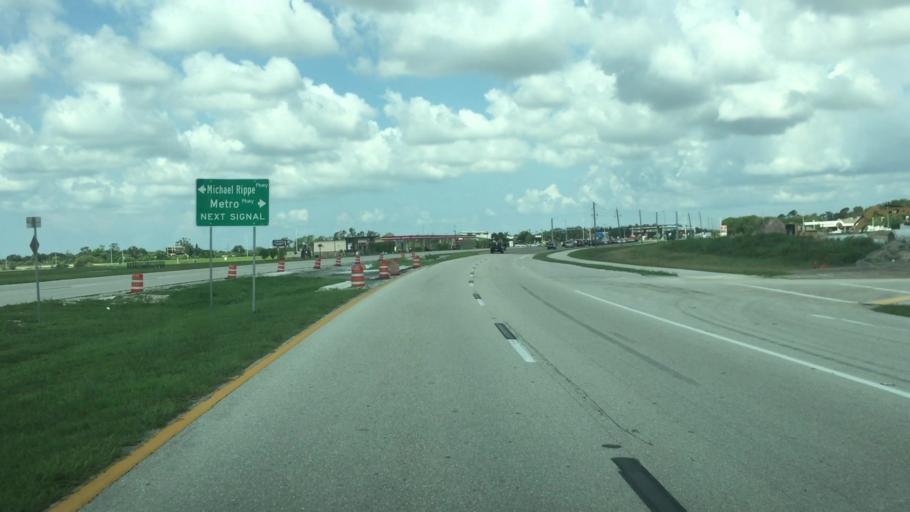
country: US
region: Florida
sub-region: Lee County
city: Villas
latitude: 26.5288
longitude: -81.8485
